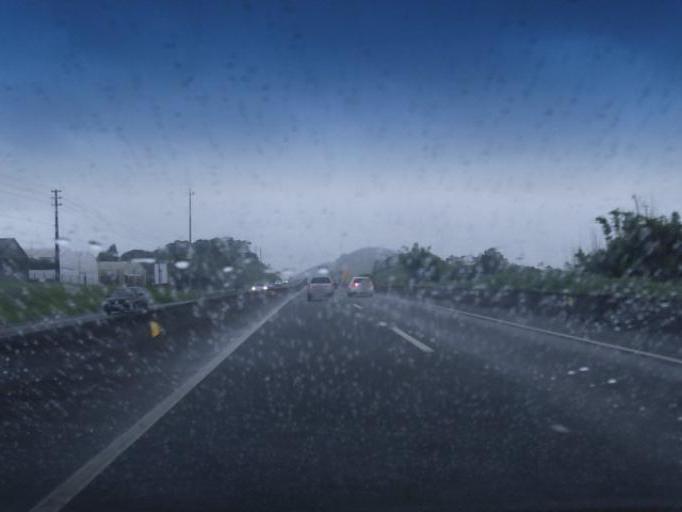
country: BR
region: Santa Catarina
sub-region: Penha
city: Penha
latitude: -26.7224
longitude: -48.7022
